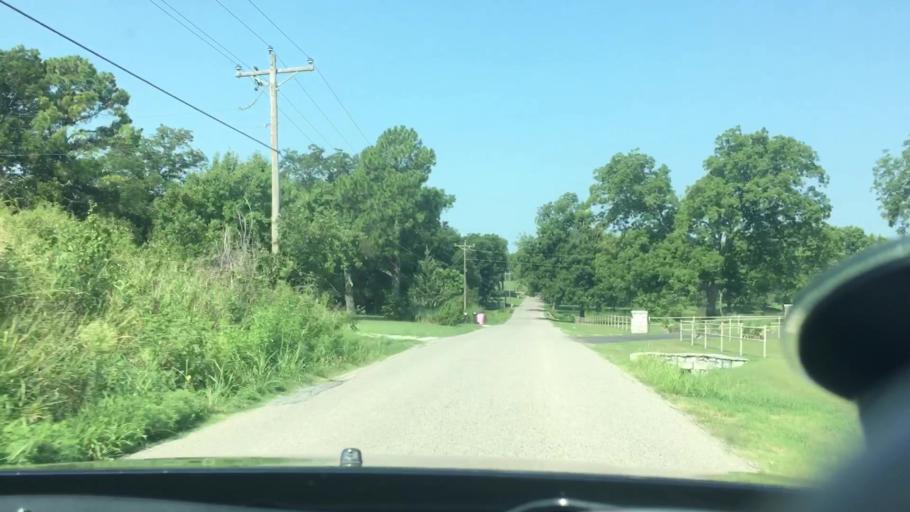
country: US
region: Oklahoma
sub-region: Bryan County
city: Durant
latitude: 34.0267
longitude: -96.3967
